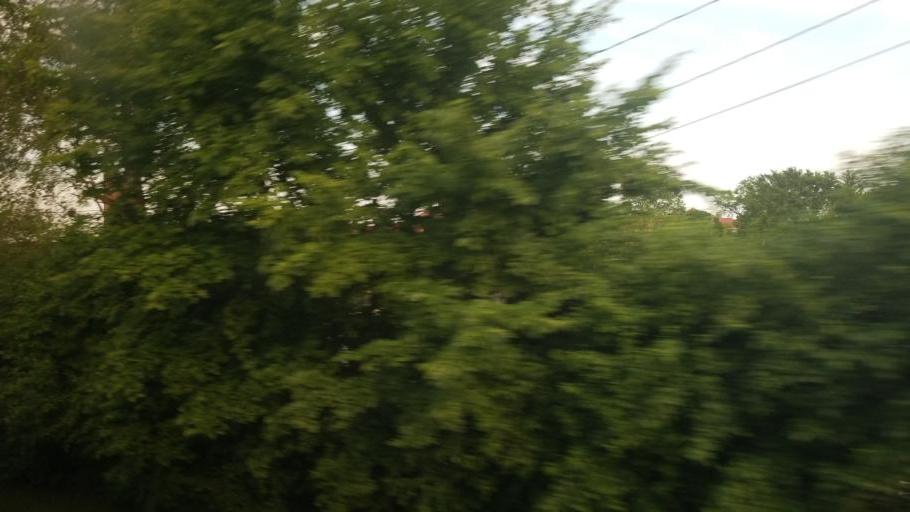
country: US
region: Illinois
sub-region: Cook County
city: La Grange
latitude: 41.8132
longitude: -87.8826
